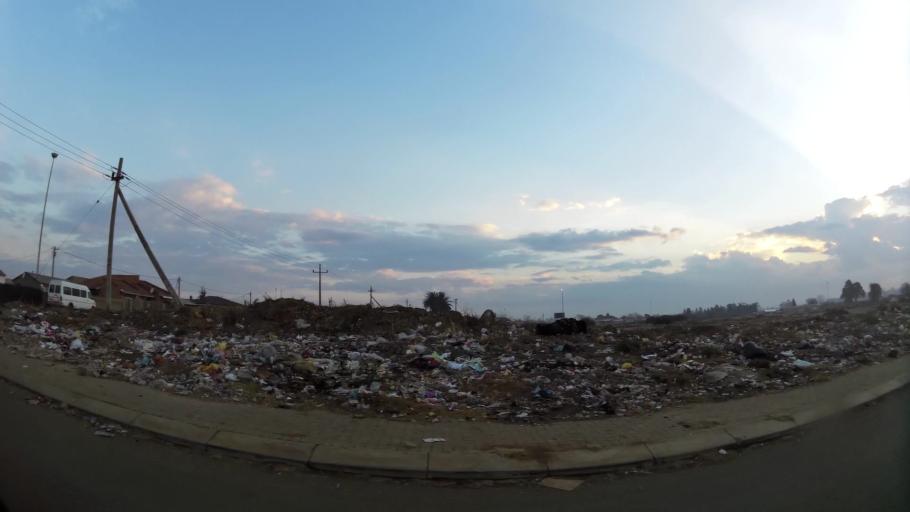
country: ZA
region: Gauteng
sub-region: City of Johannesburg Metropolitan Municipality
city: Orange Farm
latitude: -26.5472
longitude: 27.8804
